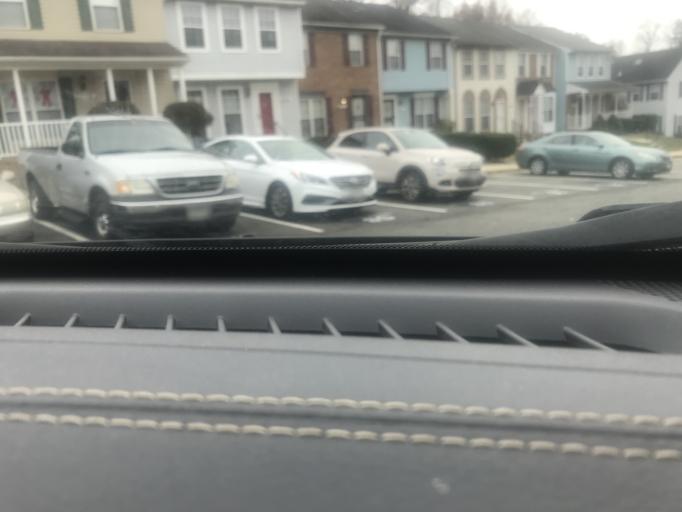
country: US
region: Maryland
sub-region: Prince George's County
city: Hillcrest Heights
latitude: 38.8151
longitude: -76.9660
